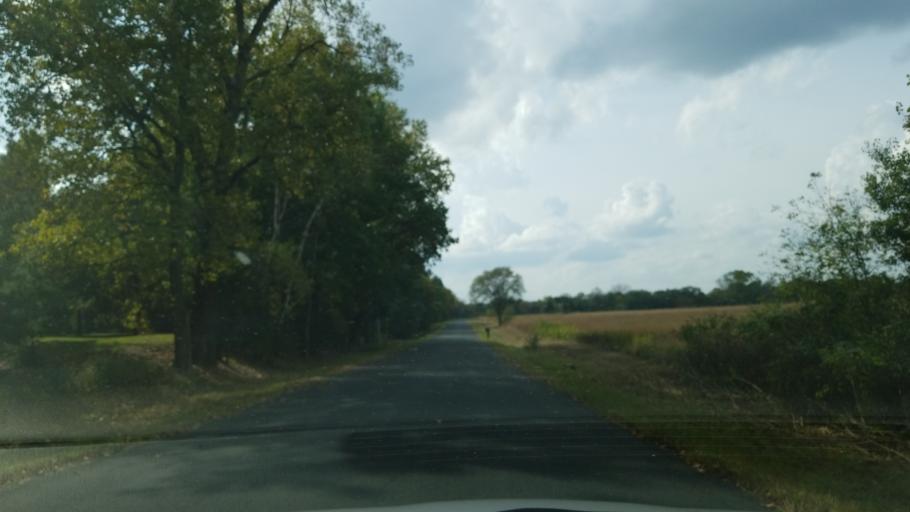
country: US
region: Minnesota
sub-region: Washington County
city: Lake Saint Croix Beach
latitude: 44.9092
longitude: -92.7411
